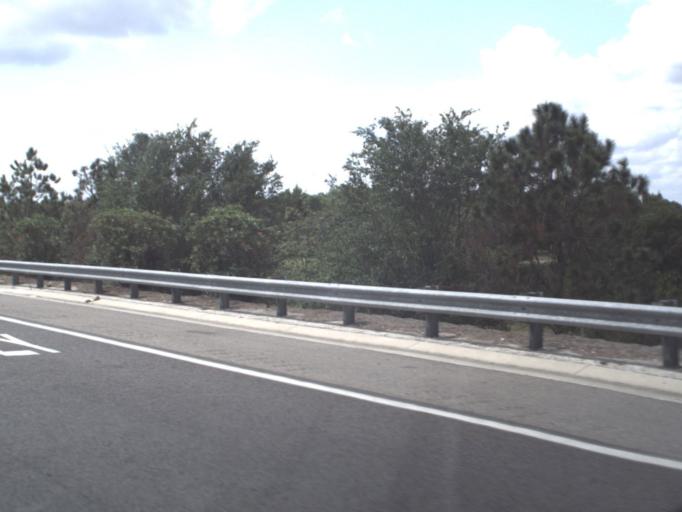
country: US
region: Florida
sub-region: Orange County
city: Paradise Heights
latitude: 28.6085
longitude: -81.5374
